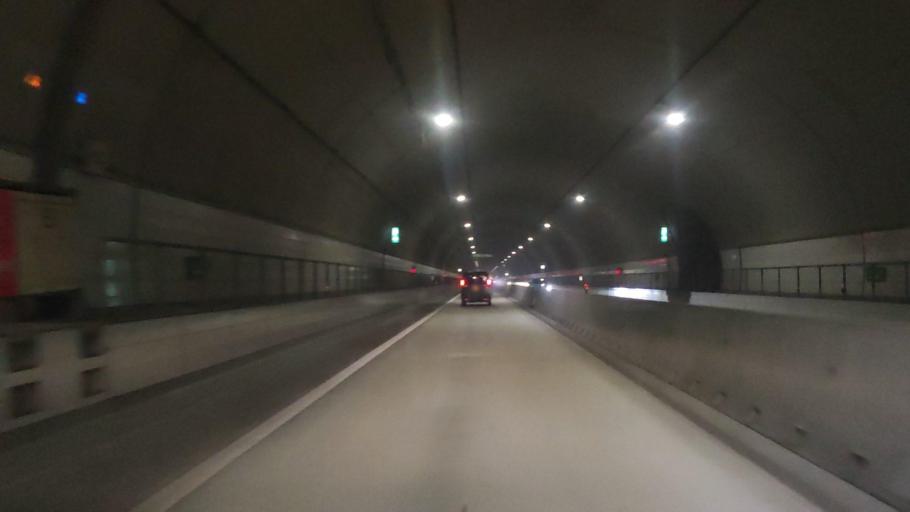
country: JP
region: Kumamoto
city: Ozu
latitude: 32.9030
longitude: 130.9474
